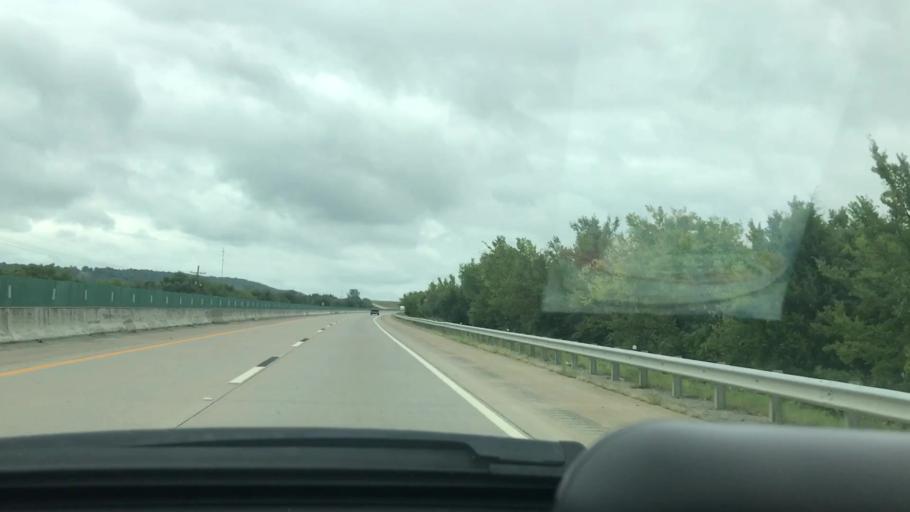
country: US
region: Oklahoma
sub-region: Pittsburg County
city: Krebs
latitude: 35.0483
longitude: -95.7097
